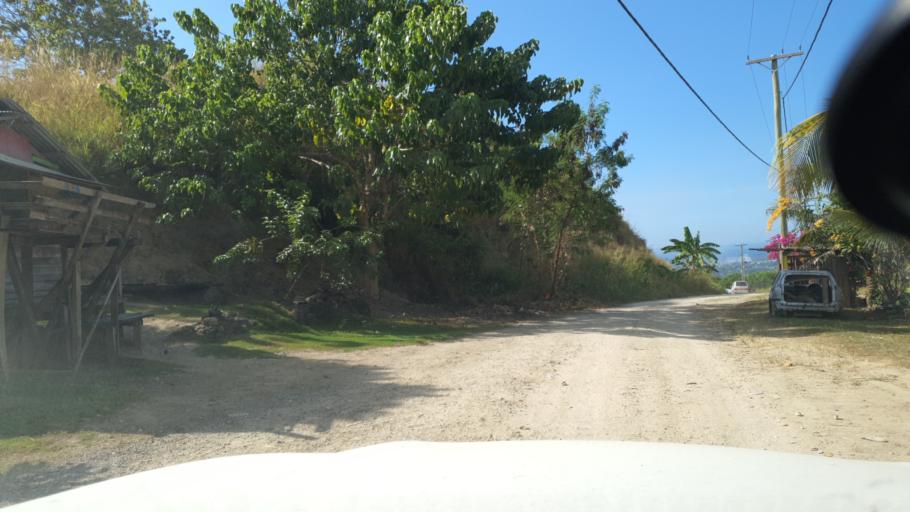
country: SB
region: Guadalcanal
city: Honiara
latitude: -9.4592
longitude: 159.9761
